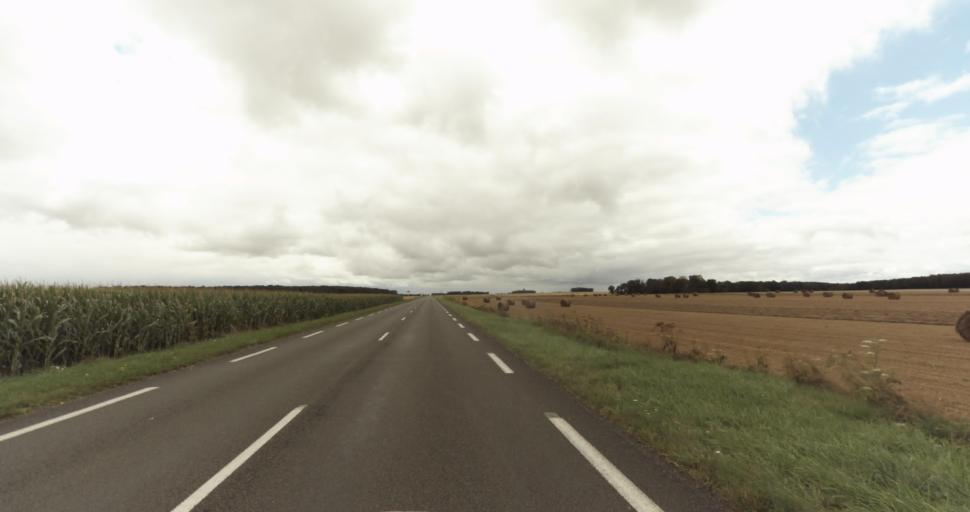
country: FR
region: Haute-Normandie
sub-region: Departement de l'Eure
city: Arnieres-sur-Iton
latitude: 48.9479
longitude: 1.1631
